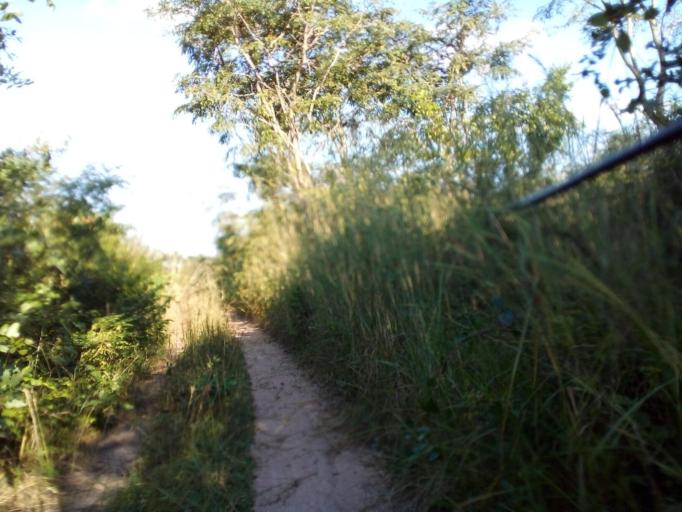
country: MZ
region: Zambezia
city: Quelimane
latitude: -17.5434
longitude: 36.8567
